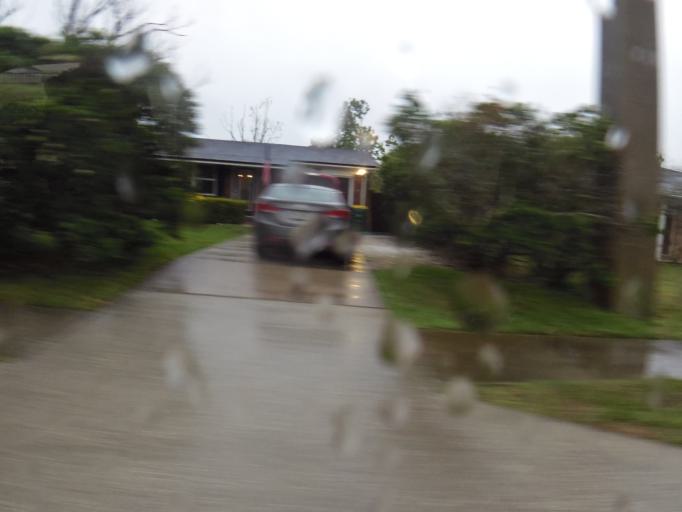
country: US
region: Florida
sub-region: Duval County
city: Jacksonville Beach
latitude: 30.2693
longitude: -81.3948
